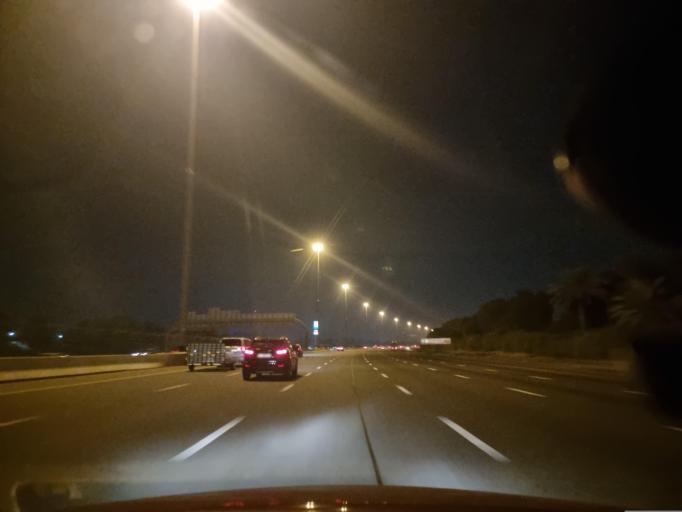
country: AE
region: Dubai
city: Dubai
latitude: 25.0615
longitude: 55.2885
